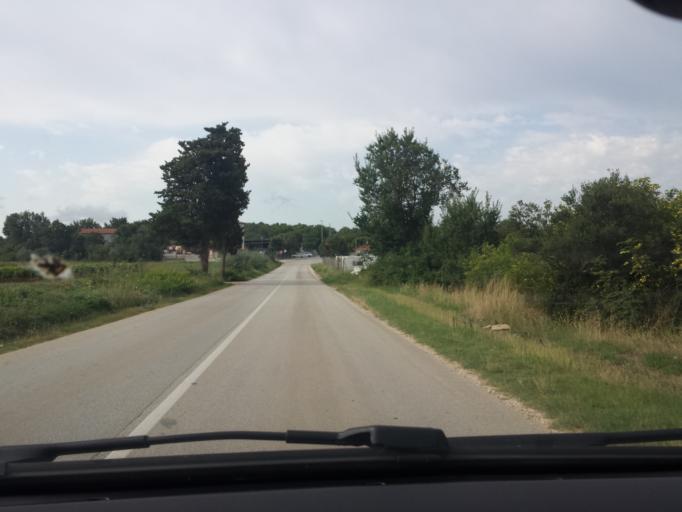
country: HR
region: Istarska
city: Galizana
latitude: 44.9080
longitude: 13.8556
